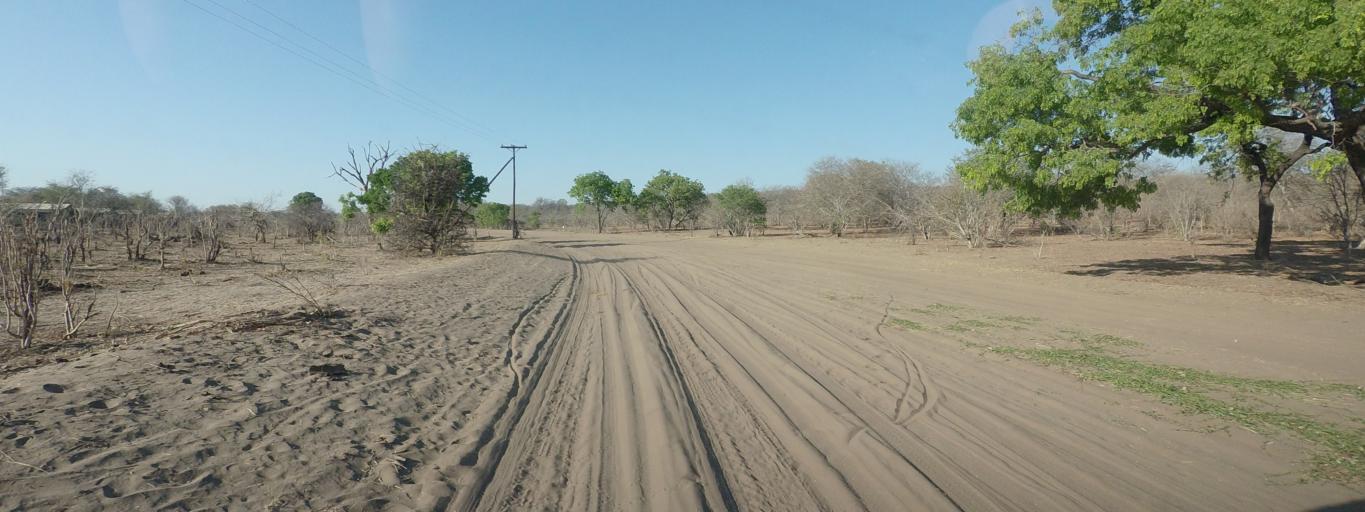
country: BW
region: North West
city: Kasane
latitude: -17.8866
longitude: 25.2300
